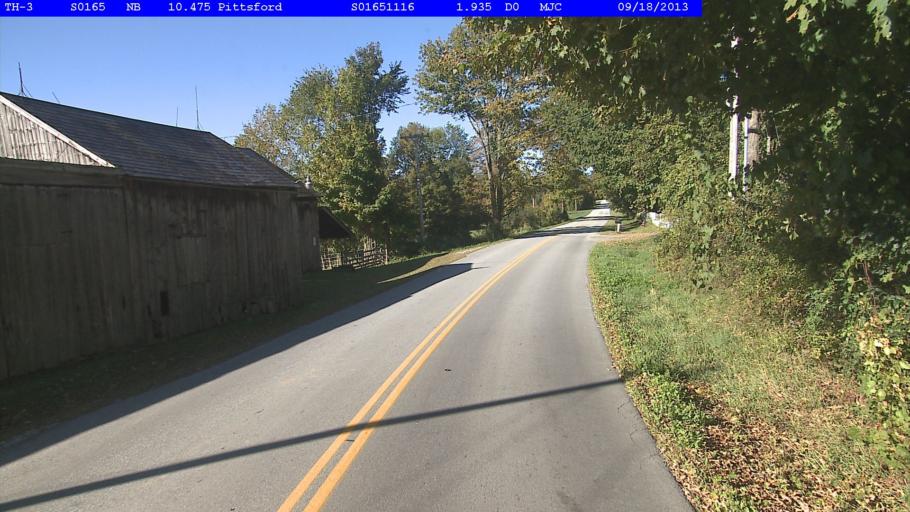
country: US
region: Vermont
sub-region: Rutland County
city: Rutland
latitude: 43.7147
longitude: -73.0070
